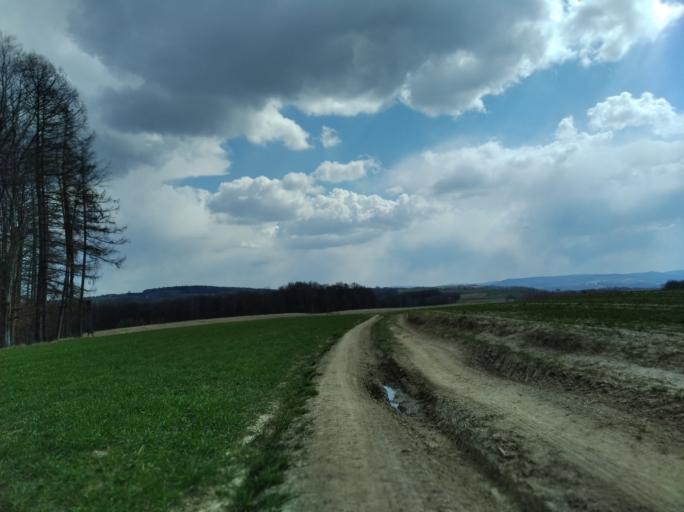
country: PL
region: Subcarpathian Voivodeship
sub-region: Powiat strzyzowski
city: Strzyzow
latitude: 49.9220
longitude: 21.7407
